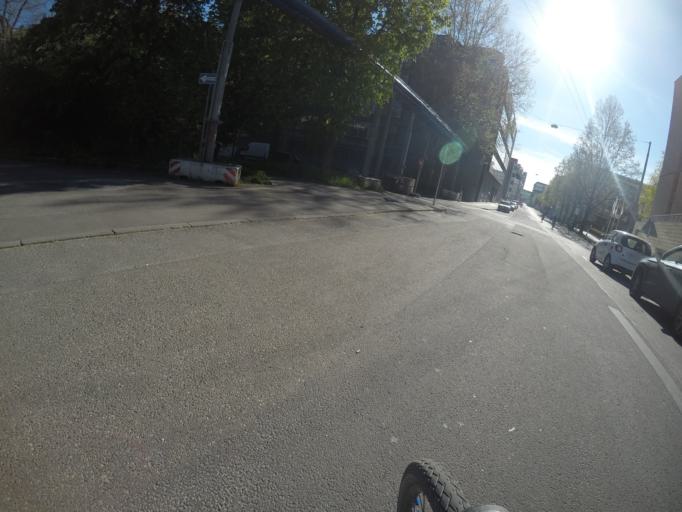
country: DE
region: Baden-Wuerttemberg
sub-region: Regierungsbezirk Stuttgart
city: Stuttgart
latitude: 48.7854
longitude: 9.1772
